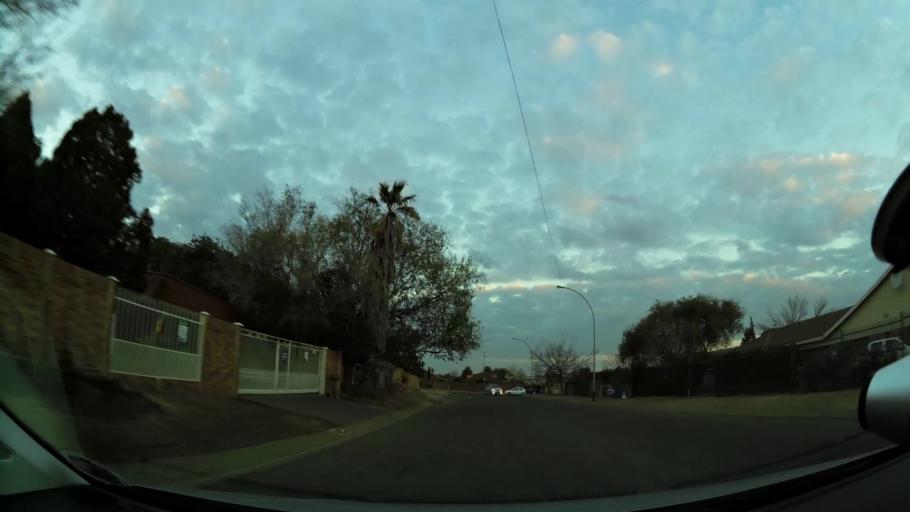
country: ZA
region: Orange Free State
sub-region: Mangaung Metropolitan Municipality
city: Bloemfontein
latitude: -29.1641
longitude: 26.1876
